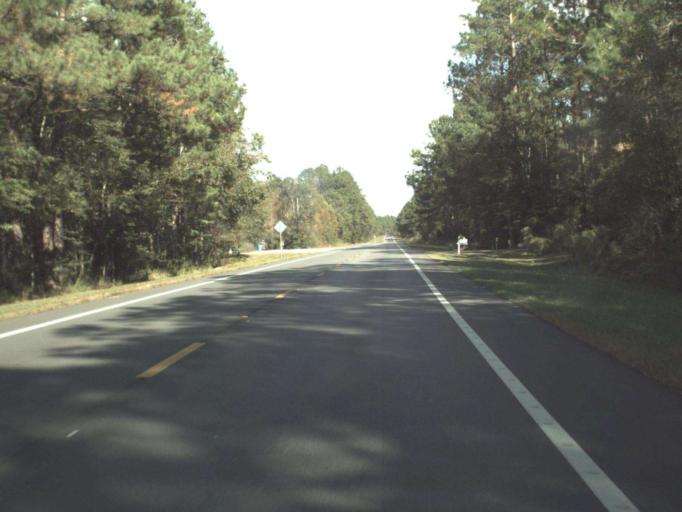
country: US
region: Florida
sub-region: Holmes County
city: Bonifay
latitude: 30.7778
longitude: -85.8006
